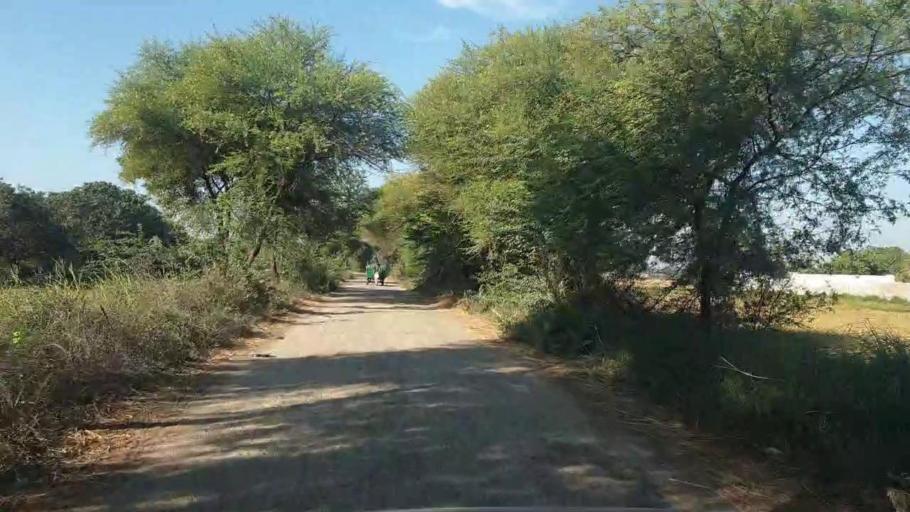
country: PK
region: Sindh
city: Talhar
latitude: 24.8912
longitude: 68.8187
